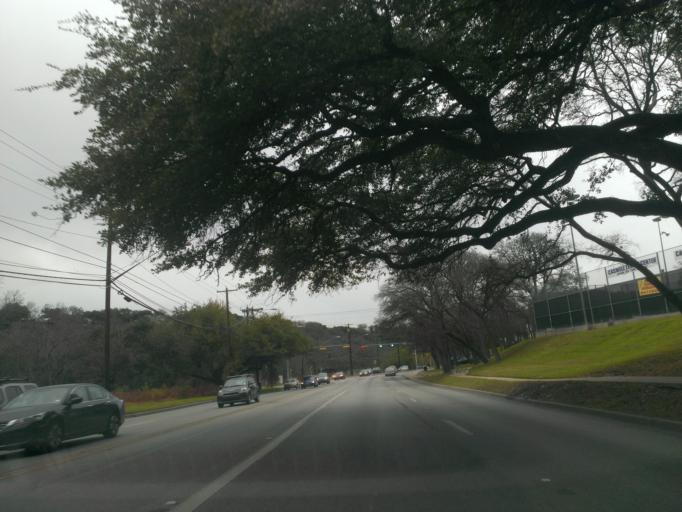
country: US
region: Texas
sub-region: Travis County
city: Austin
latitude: 30.2875
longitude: -97.7530
